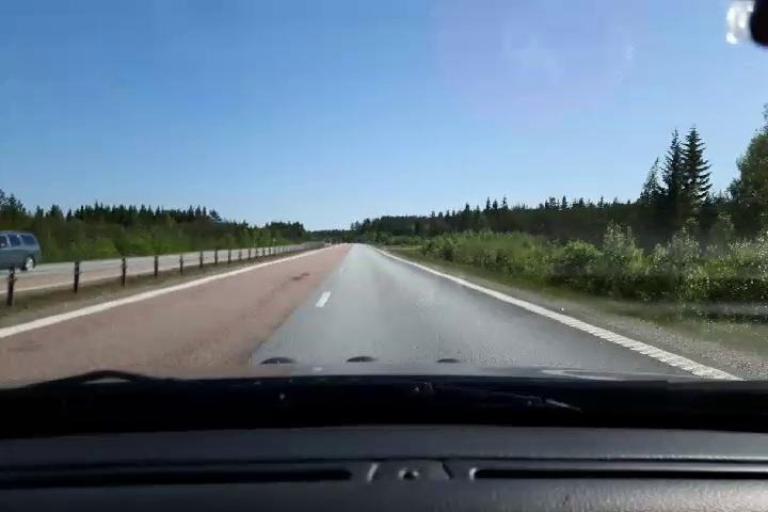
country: SE
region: Gaevleborg
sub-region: Soderhamns Kommun
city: Soderhamn
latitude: 61.4238
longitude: 16.9844
